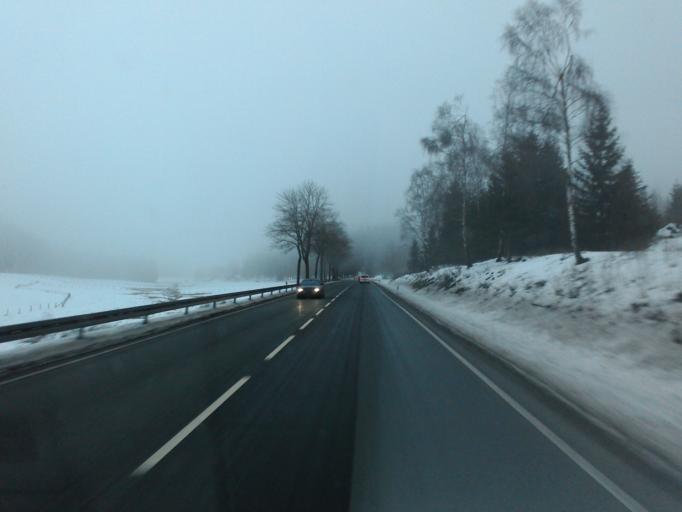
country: DE
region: North Rhine-Westphalia
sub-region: Regierungsbezirk Arnsberg
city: Winterberg
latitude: 51.2207
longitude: 8.5415
